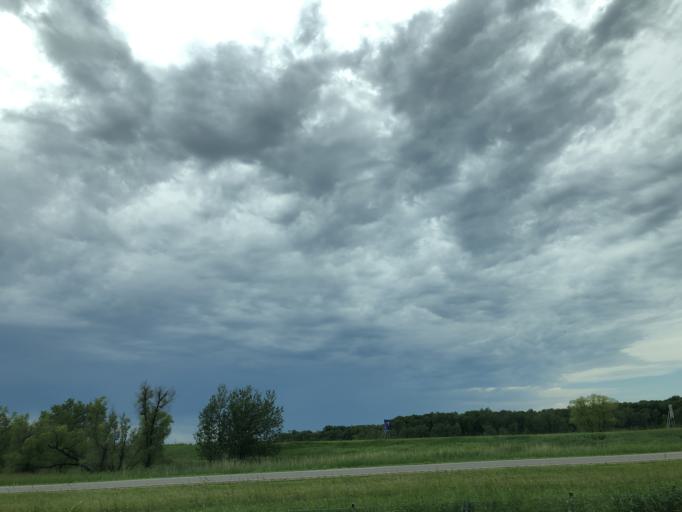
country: US
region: Minnesota
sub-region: Stearns County
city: Saint Joseph
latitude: 45.5167
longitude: -94.2861
